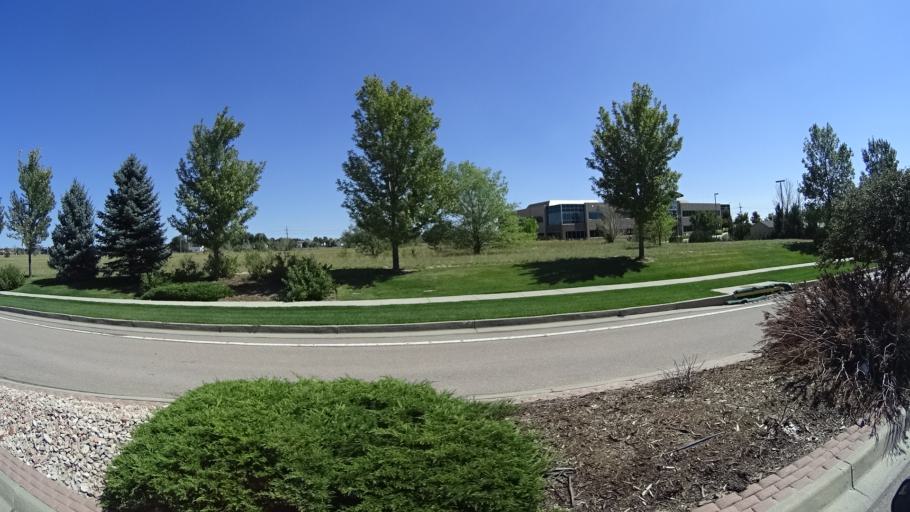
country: US
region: Colorado
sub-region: El Paso County
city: Cimarron Hills
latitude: 38.8421
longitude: -104.7244
